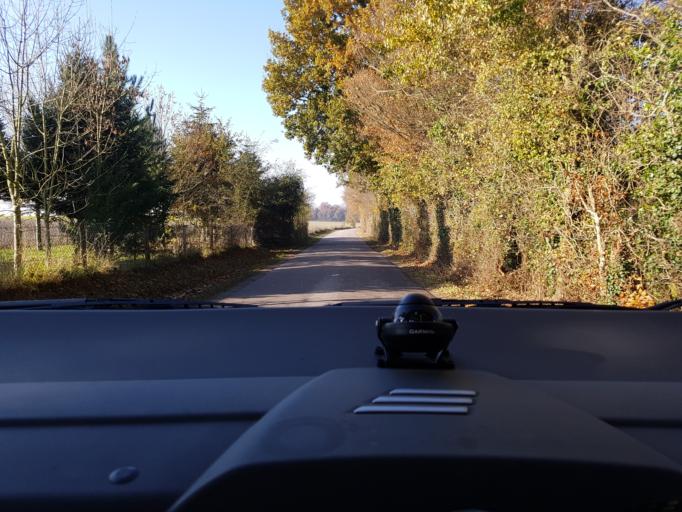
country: FR
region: Lower Normandy
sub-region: Departement du Calvados
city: Clinchamps-sur-Orne
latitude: 49.0075
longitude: -0.3965
